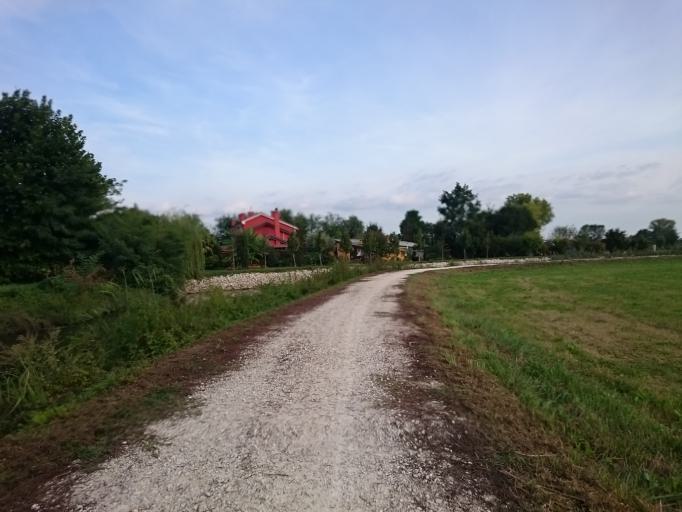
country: IT
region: Veneto
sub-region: Provincia di Vicenza
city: Camisano Vicentino
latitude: 45.5322
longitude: 11.6935
